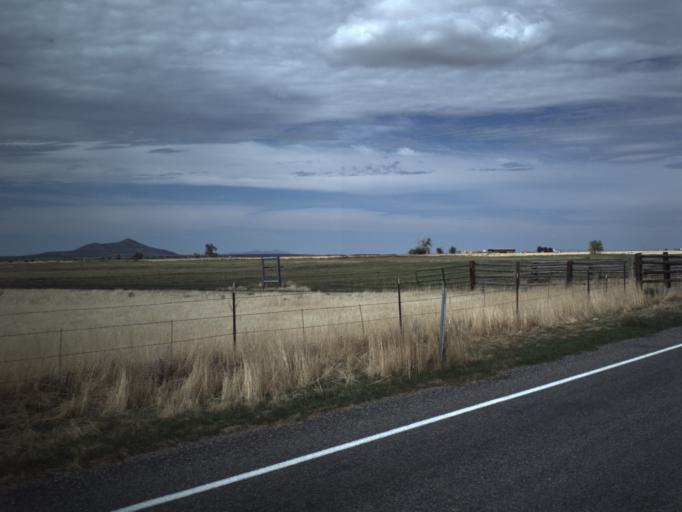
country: US
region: Utah
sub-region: Millard County
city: Fillmore
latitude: 39.0372
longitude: -112.4099
